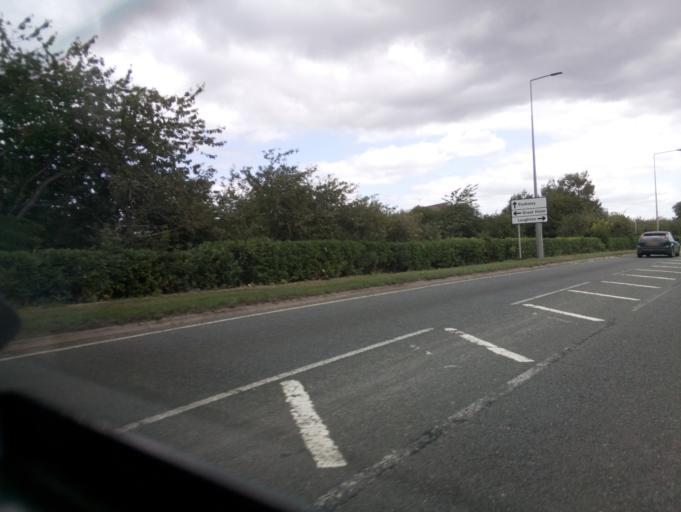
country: GB
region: England
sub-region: Milton Keynes
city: Shenley Church End
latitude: 52.0310
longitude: -0.7929
